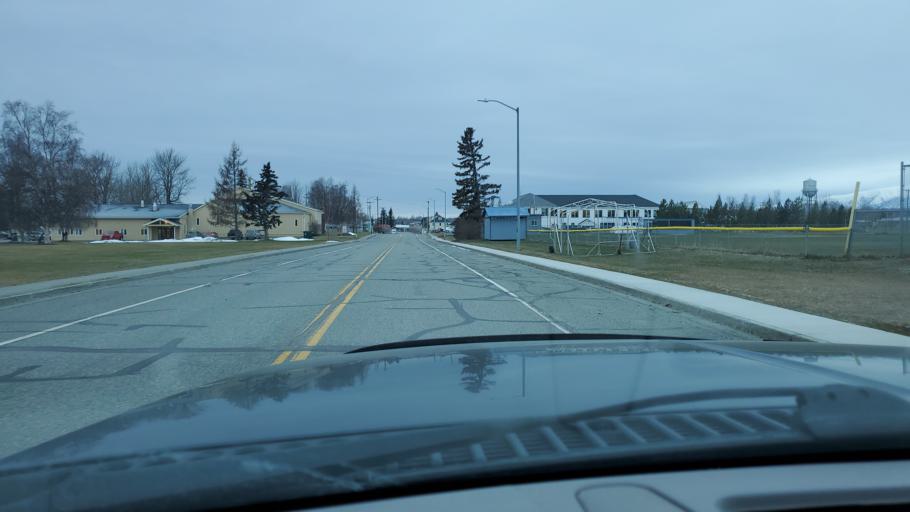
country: US
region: Alaska
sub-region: Matanuska-Susitna Borough
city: Palmer
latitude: 61.5988
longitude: -149.1038
